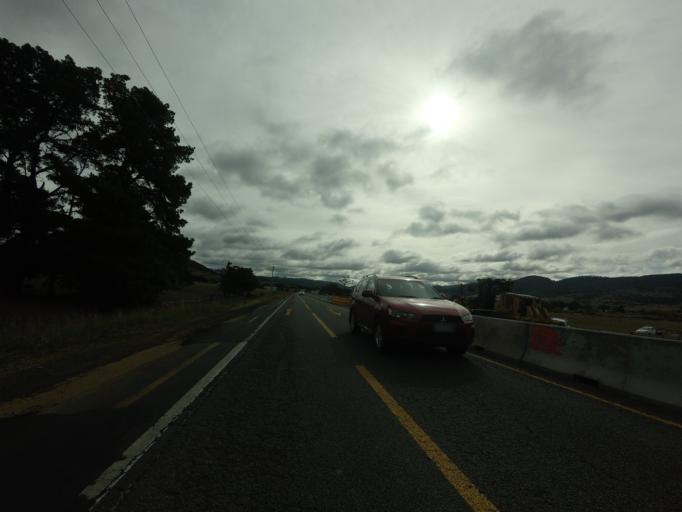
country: AU
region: Tasmania
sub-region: Brighton
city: Bridgewater
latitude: -42.6620
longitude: 147.2479
